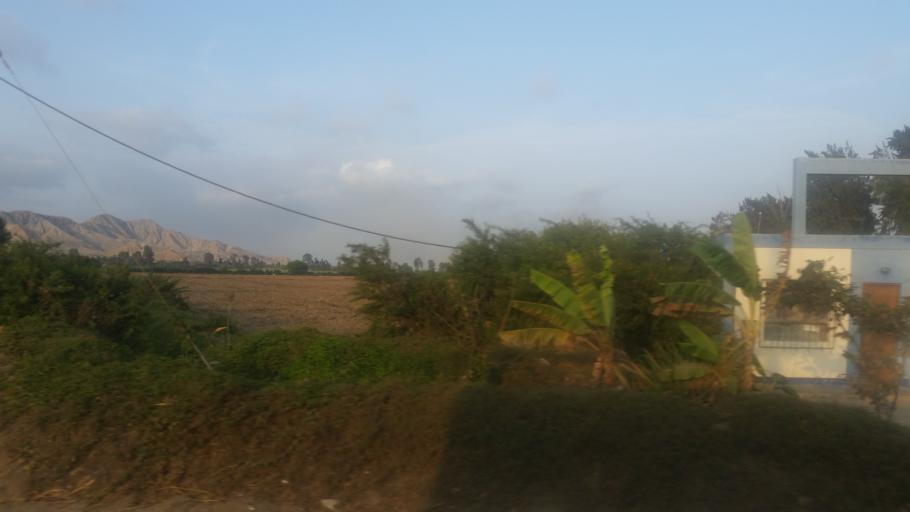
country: PE
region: La Libertad
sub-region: Ascope
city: Paijan
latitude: -7.7484
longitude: -79.2835
